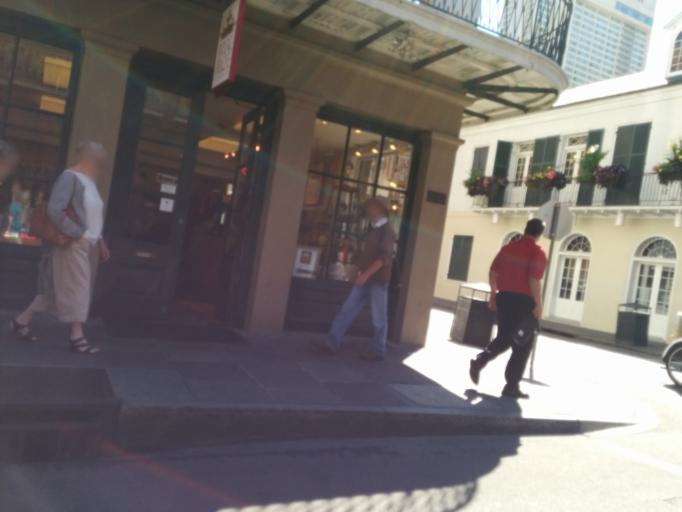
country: US
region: Louisiana
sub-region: Orleans Parish
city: New Orleans
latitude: 29.9549
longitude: -90.0673
